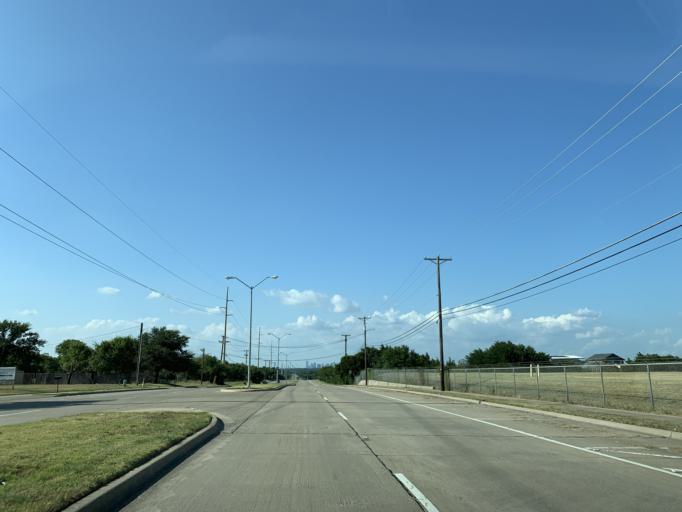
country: US
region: Texas
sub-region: Dallas County
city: Lancaster
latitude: 32.6547
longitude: -96.8056
